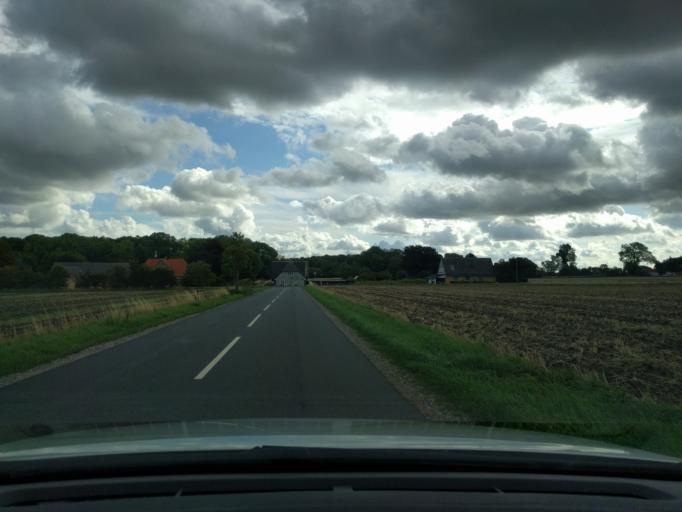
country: DK
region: South Denmark
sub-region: Nyborg Kommune
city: Ullerslev
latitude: 55.3912
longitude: 10.6642
